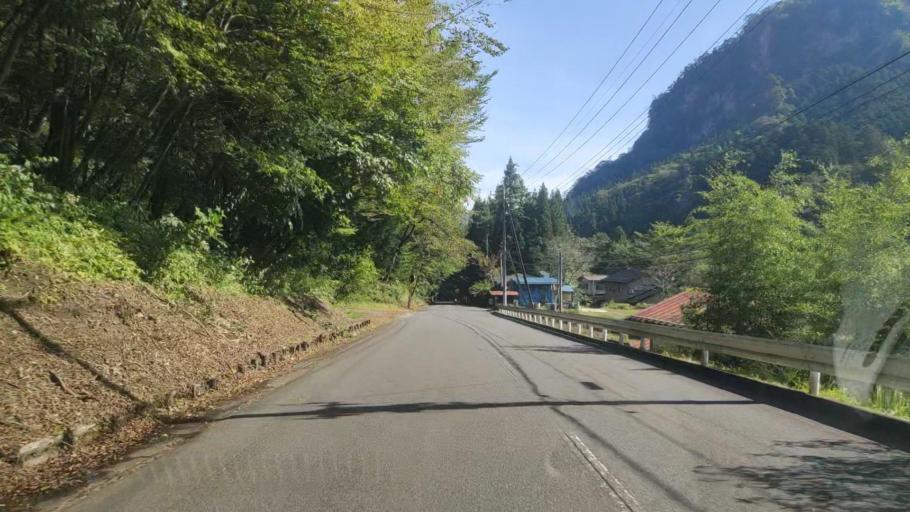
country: JP
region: Gunma
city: Nakanojomachi
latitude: 36.6114
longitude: 138.7379
